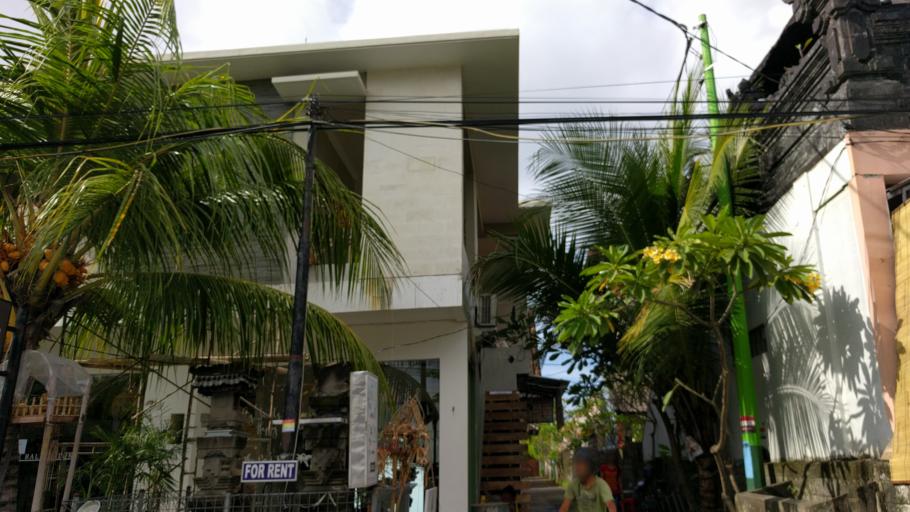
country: ID
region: Bali
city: Kuta
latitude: -8.6815
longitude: 115.1608
